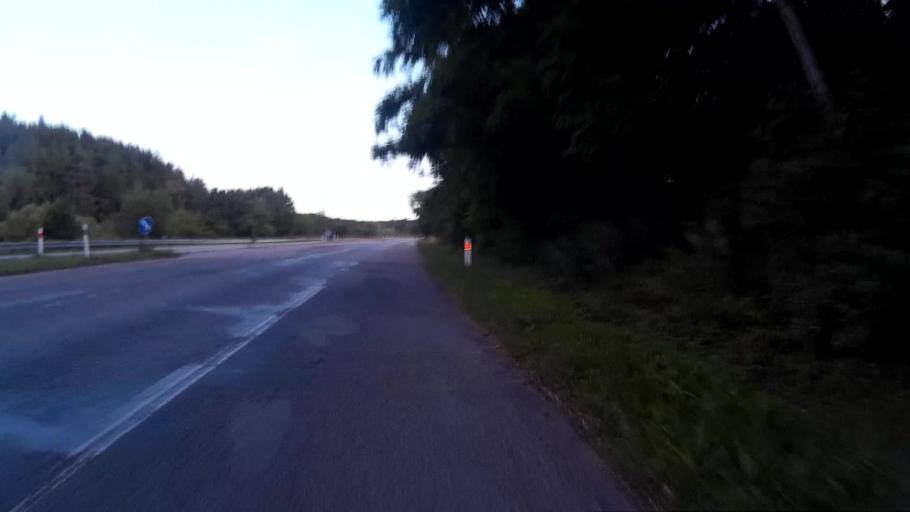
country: CZ
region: South Moravian
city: Troubsko
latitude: 49.2054
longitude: 16.5195
